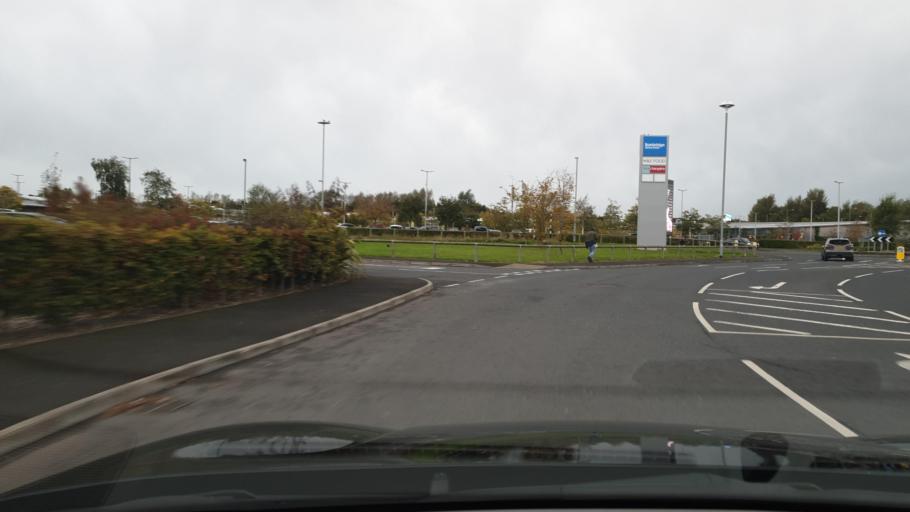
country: GB
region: Northern Ireland
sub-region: Banbridge District
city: Banbridge
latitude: 54.3332
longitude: -6.2741
